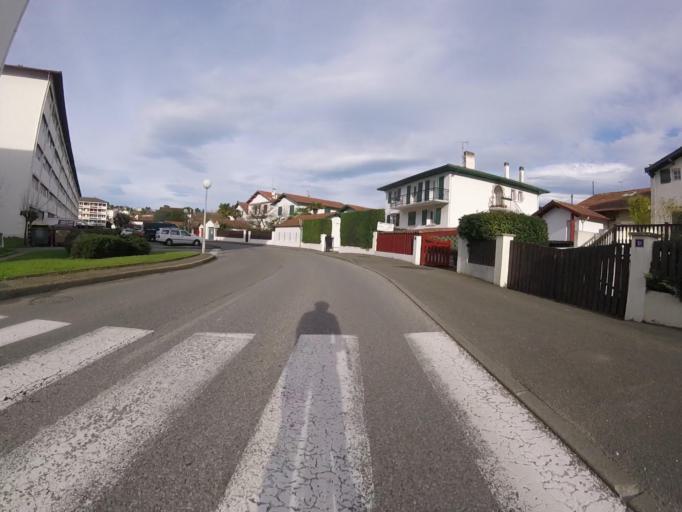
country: FR
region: Aquitaine
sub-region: Departement des Pyrenees-Atlantiques
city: Saint-Jean-de-Luz
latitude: 43.3807
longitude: -1.6627
